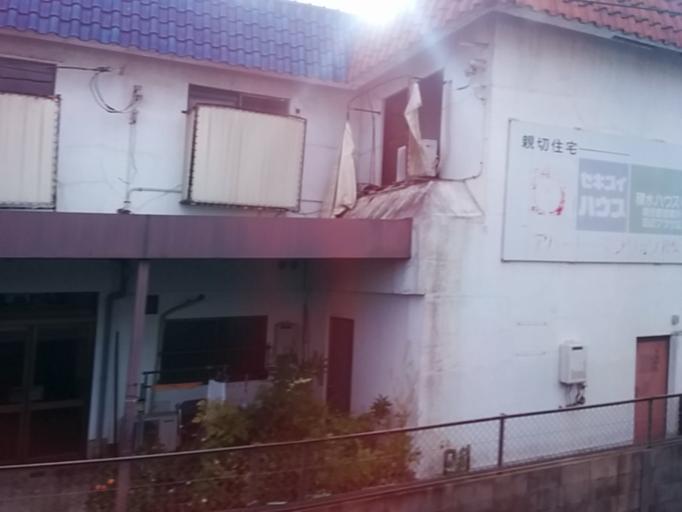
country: JP
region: Kyoto
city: Tanabe
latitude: 34.8194
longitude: 135.7728
